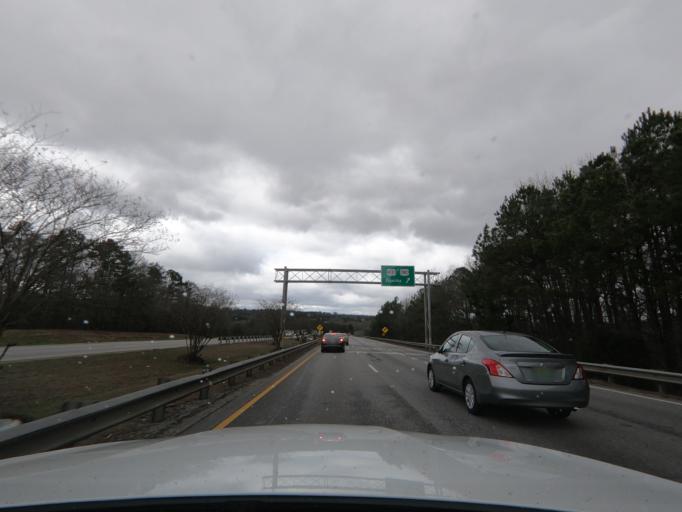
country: US
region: Alabama
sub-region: Russell County
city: Phenix City
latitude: 32.4910
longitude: -85.0288
